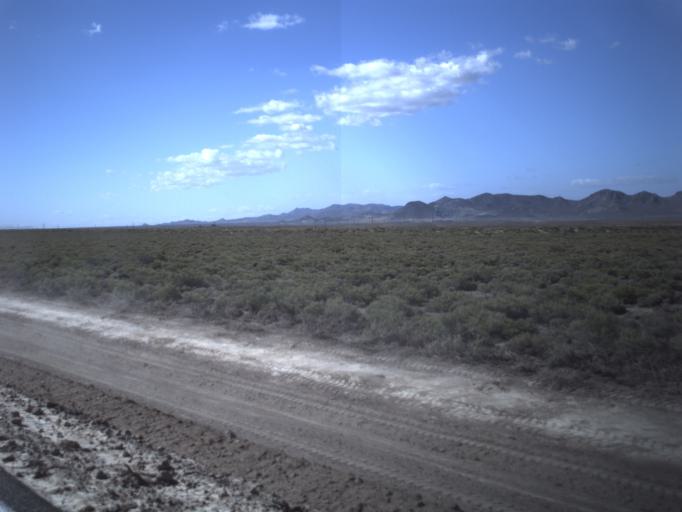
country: US
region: Utah
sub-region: Beaver County
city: Milford
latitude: 38.5182
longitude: -112.9912
